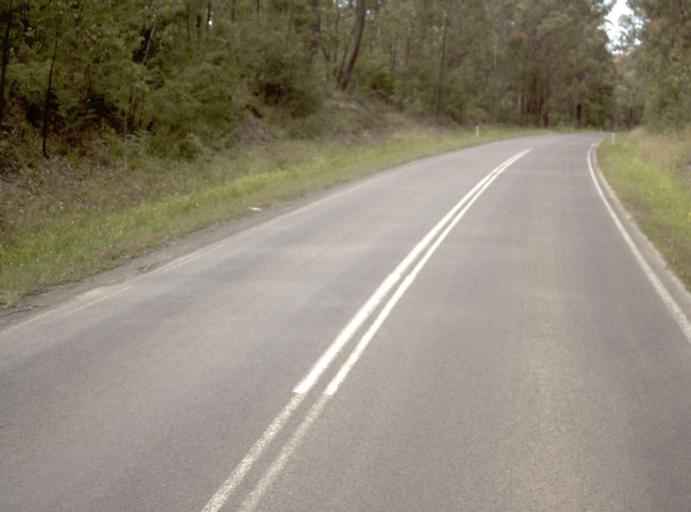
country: AU
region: Victoria
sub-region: Latrobe
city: Traralgon
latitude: -38.0936
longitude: 146.4408
